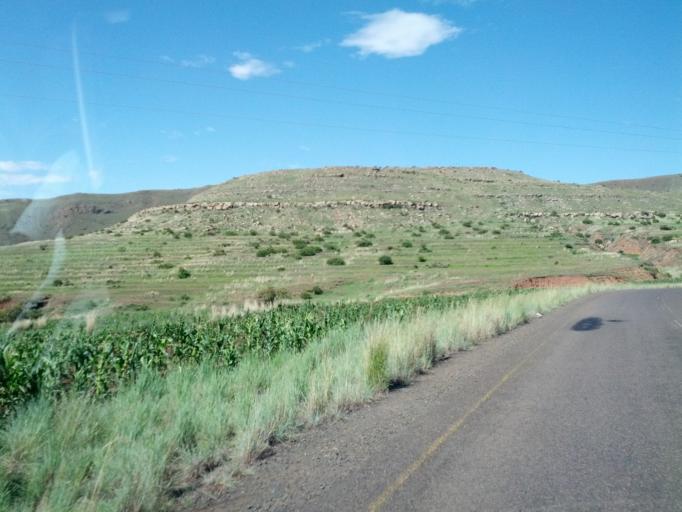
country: LS
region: Qacha's Nek
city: Qacha's Nek
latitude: -30.0666
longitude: 28.5518
